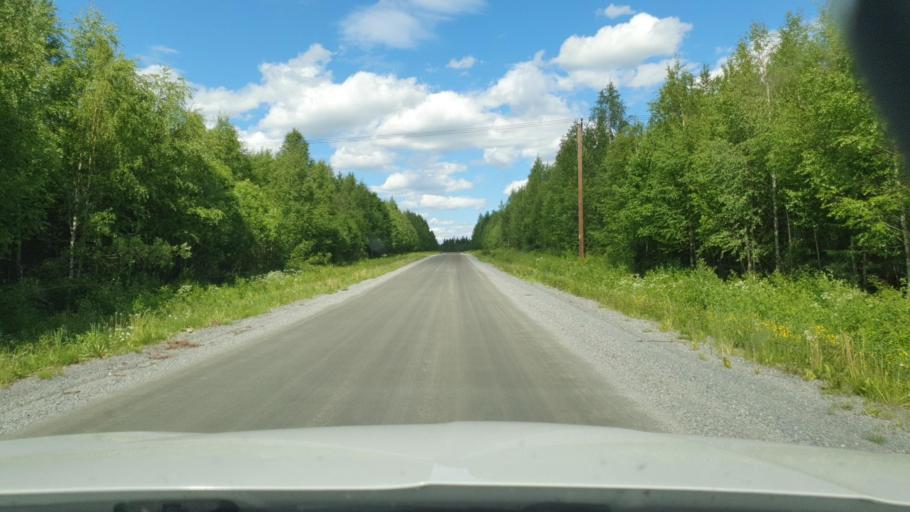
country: SE
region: Vaesterbotten
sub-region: Skelleftea Kommun
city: Forsbacka
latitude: 64.8167
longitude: 20.4937
